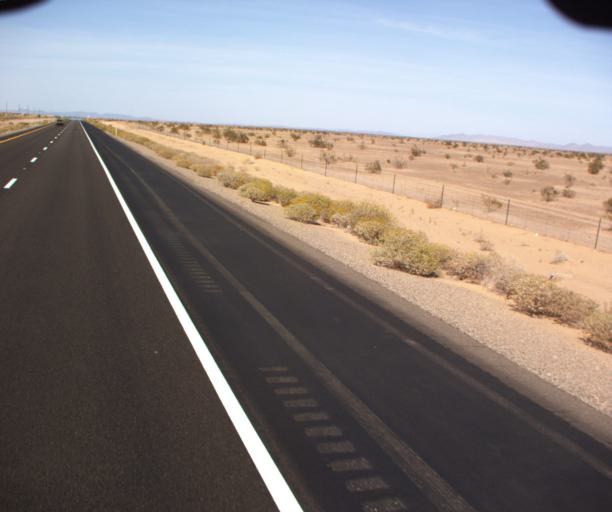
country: US
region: Arizona
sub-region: Yuma County
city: Somerton
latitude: 32.5216
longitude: -114.5617
